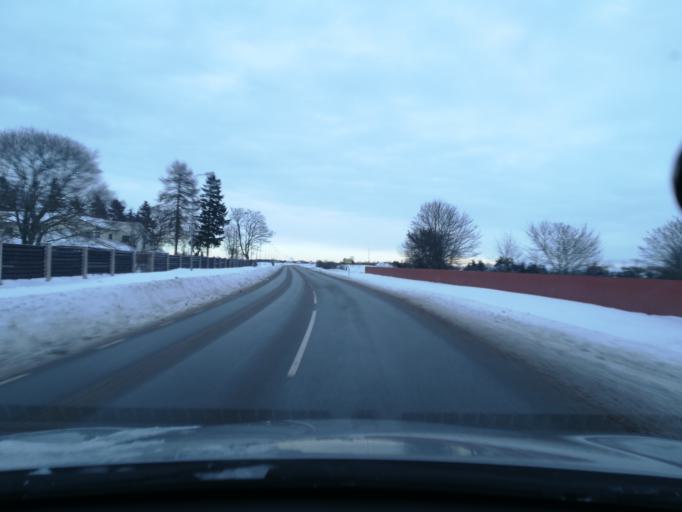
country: EE
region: Harju
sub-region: Harku vald
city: Tabasalu
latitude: 59.4484
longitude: 24.4654
